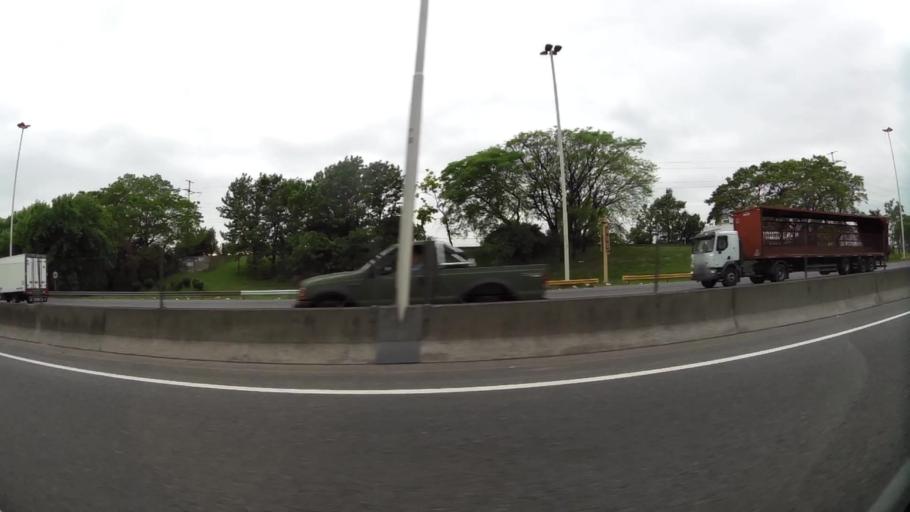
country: AR
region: Buenos Aires F.D.
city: Villa Lugano
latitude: -34.7065
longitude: -58.5016
